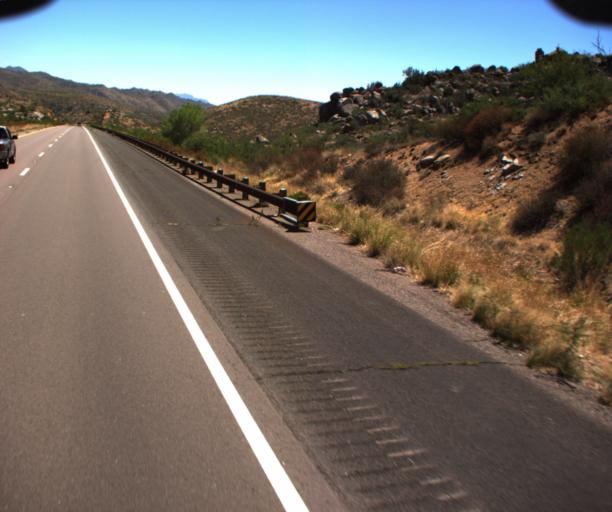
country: US
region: Arizona
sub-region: Gila County
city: Tonto Basin
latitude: 33.8470
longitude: -111.4700
